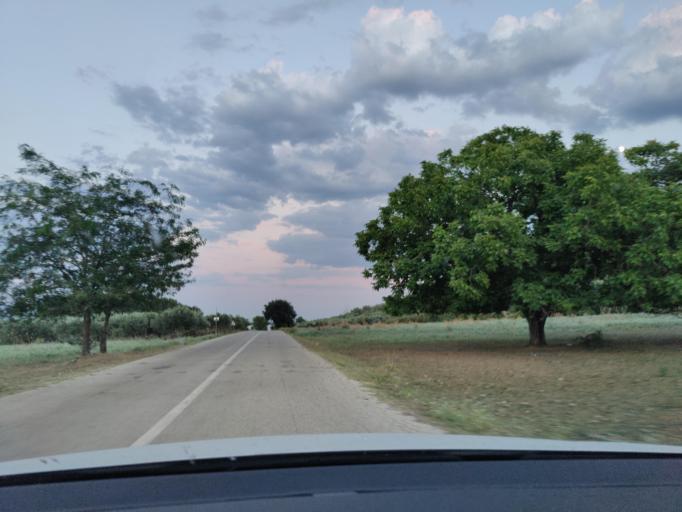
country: GR
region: Central Macedonia
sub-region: Nomos Serron
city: Chrysochorafa
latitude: 41.1625
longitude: 23.1845
